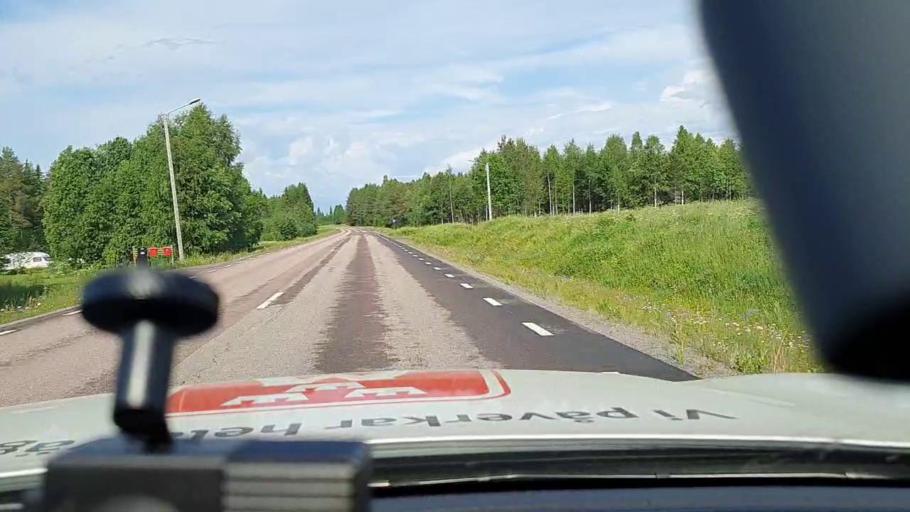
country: SE
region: Norrbotten
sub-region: Alvsbyns Kommun
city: AElvsbyn
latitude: 66.0209
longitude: 21.1358
